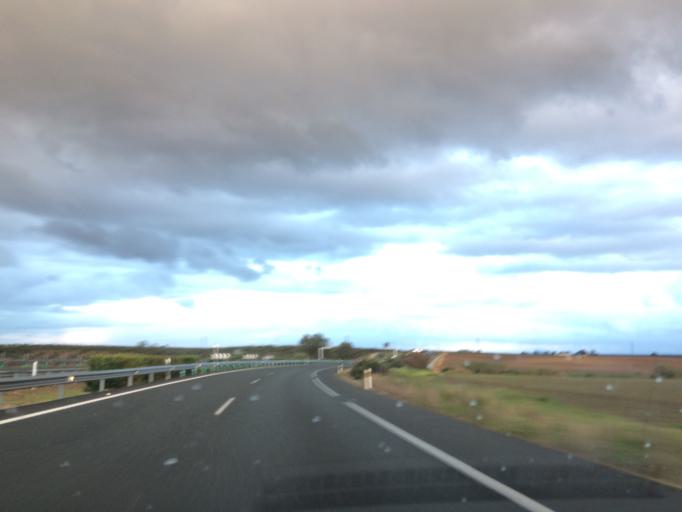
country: ES
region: Andalusia
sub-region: Provincia de Sevilla
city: Mairena del Alcor
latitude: 37.3221
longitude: -5.7709
